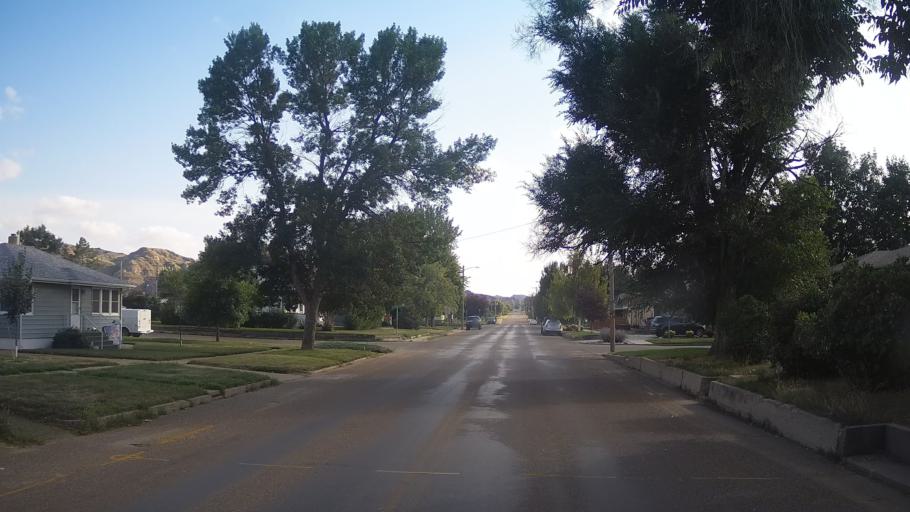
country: US
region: Montana
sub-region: Dawson County
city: Glendive
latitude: 47.0965
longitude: -104.7114
